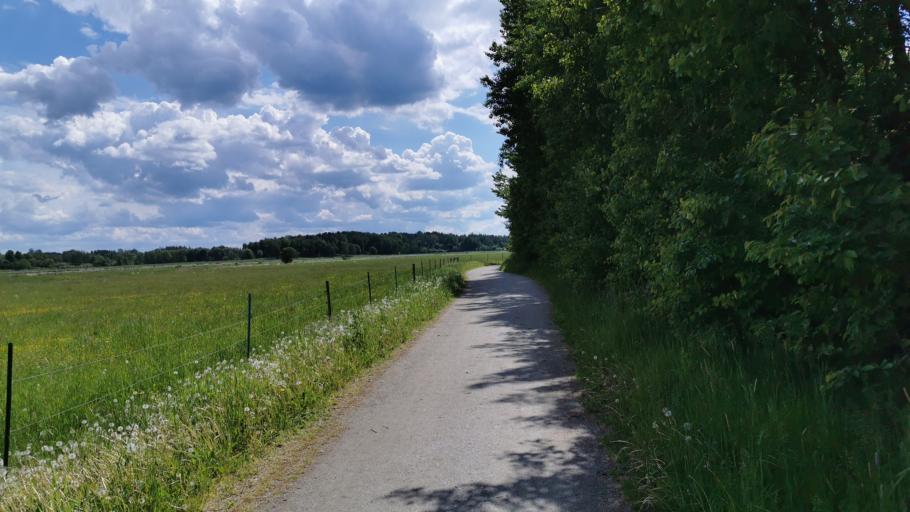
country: SE
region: OErebro
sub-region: Orebro Kommun
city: Orebro
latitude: 59.3045
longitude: 15.2107
